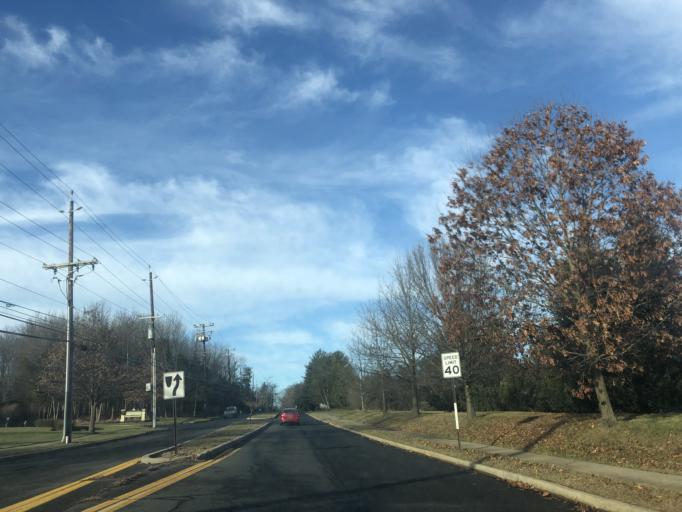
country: US
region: New Jersey
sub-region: Middlesex County
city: Heathcote
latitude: 40.3802
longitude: -74.5835
